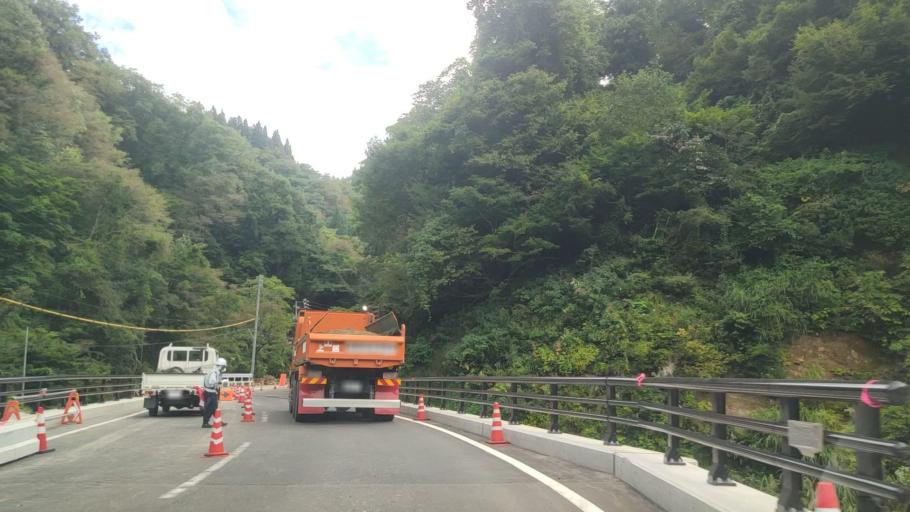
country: JP
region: Nagano
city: Iiyama
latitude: 36.9027
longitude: 138.3156
